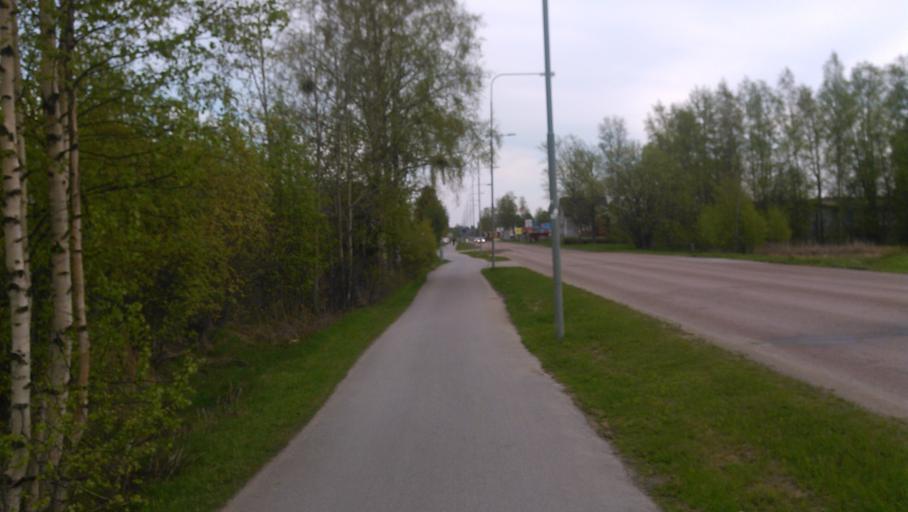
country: SE
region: Vaesterbotten
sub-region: Umea Kommun
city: Umea
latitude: 63.8085
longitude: 20.2715
